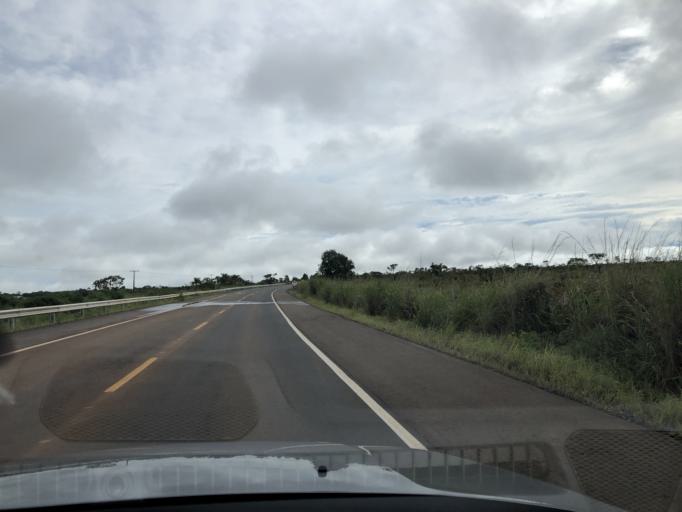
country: BR
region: Federal District
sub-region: Brasilia
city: Brasilia
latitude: -15.6281
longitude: -48.0743
